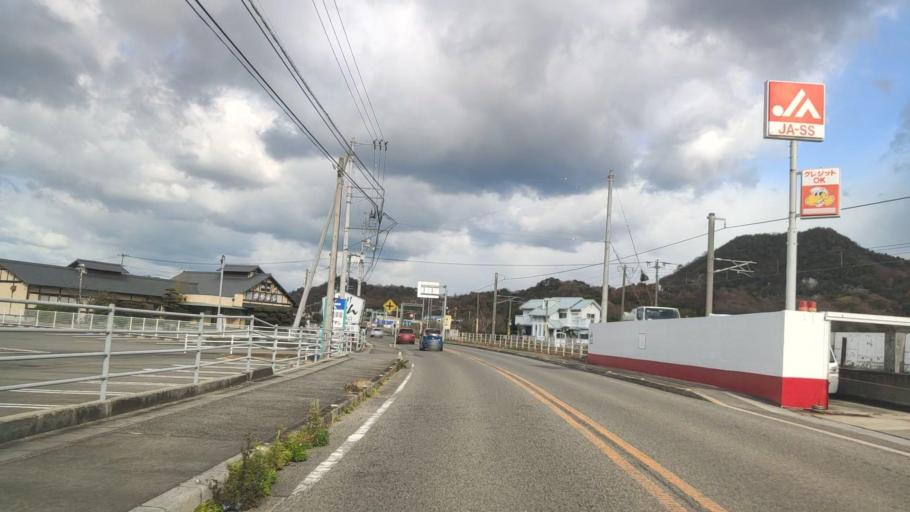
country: JP
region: Ehime
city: Hojo
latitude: 33.9840
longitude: 132.7785
